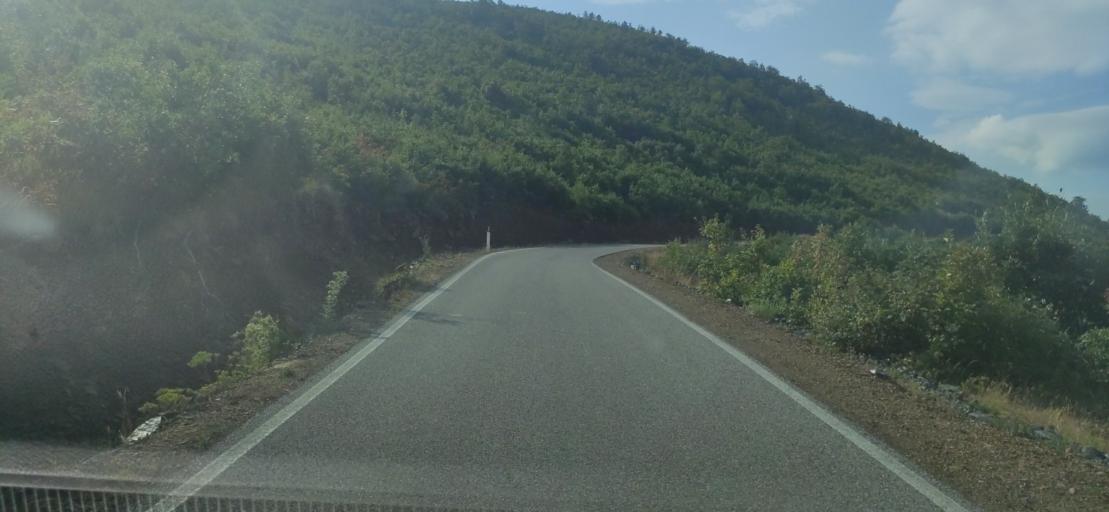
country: AL
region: Shkoder
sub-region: Rrethi i Pukes
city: Iballe
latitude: 42.1706
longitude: 20.0026
